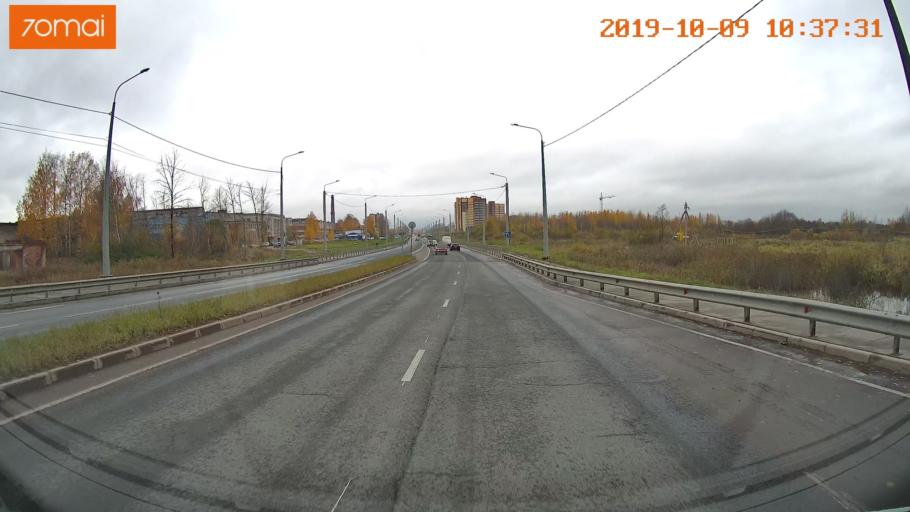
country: RU
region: Vologda
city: Vologda
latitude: 59.2354
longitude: 39.8608
